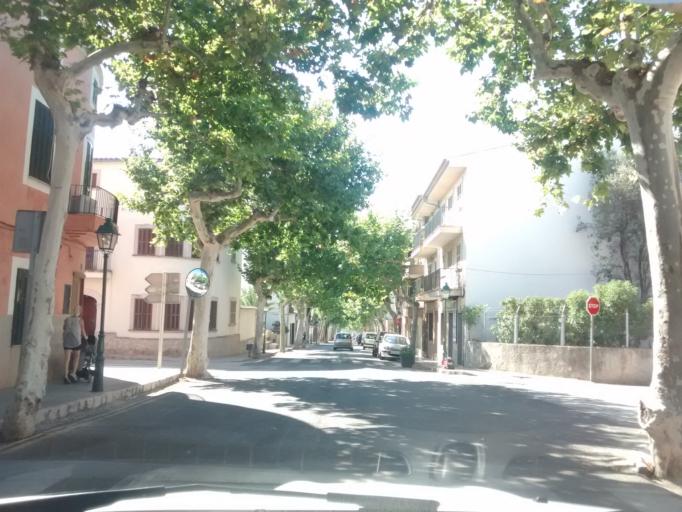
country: ES
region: Balearic Islands
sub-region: Illes Balears
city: Alaro
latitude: 39.7043
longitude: 2.7921
